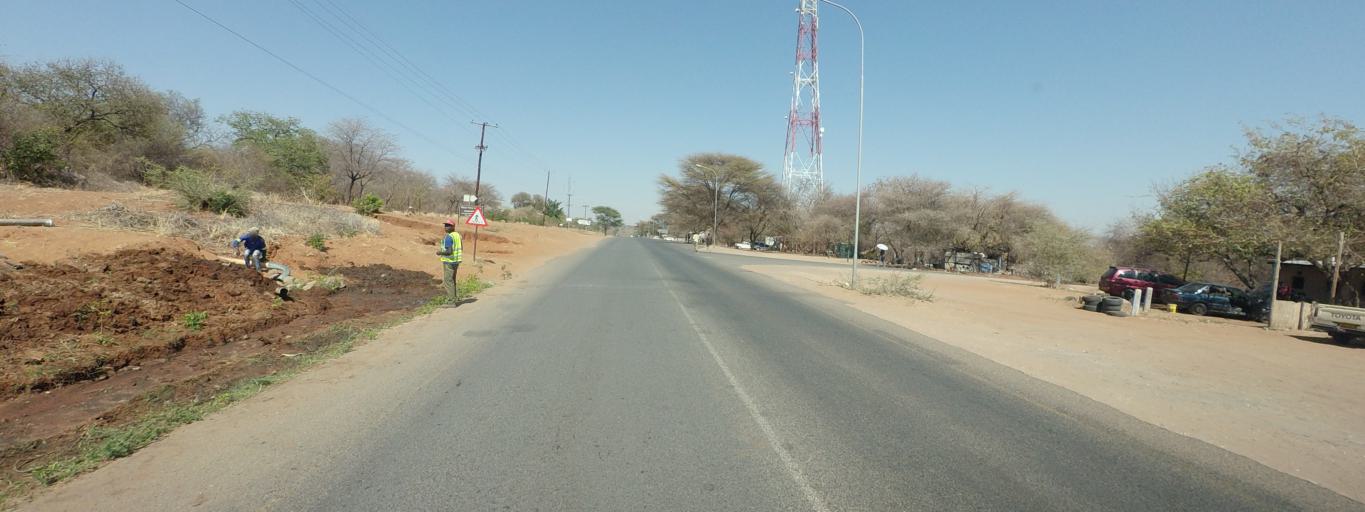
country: BW
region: North West
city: Kasane
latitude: -17.7988
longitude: 25.2309
